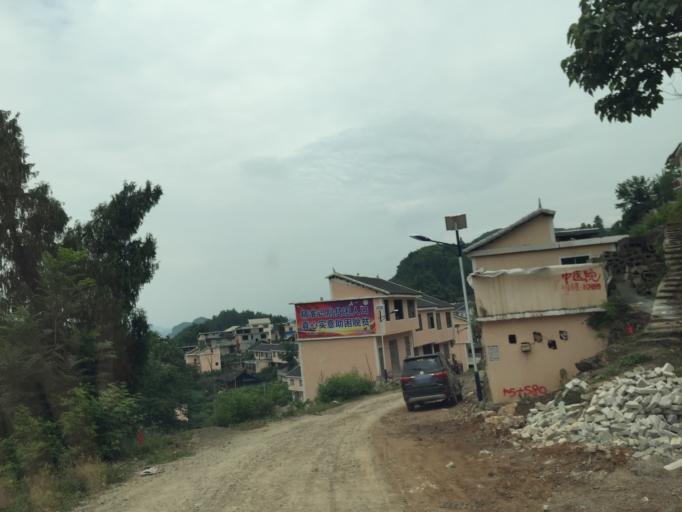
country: CN
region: Guizhou Sheng
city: Tongjing
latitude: 28.3695
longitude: 108.2355
